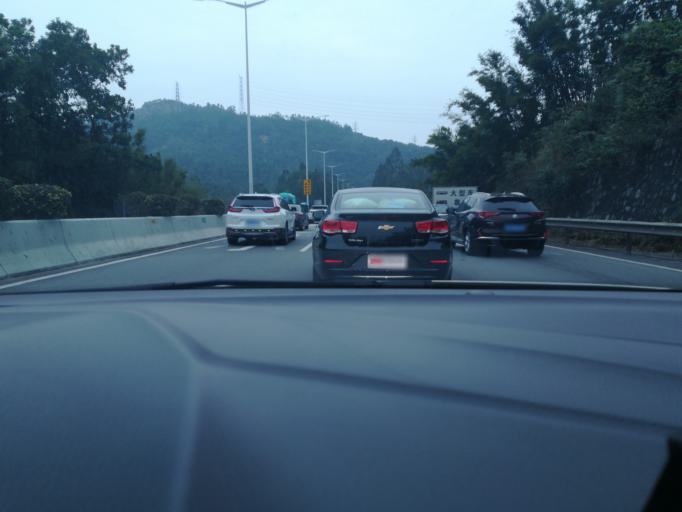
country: CN
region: Guangdong
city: Longdong
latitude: 23.2231
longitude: 113.3578
